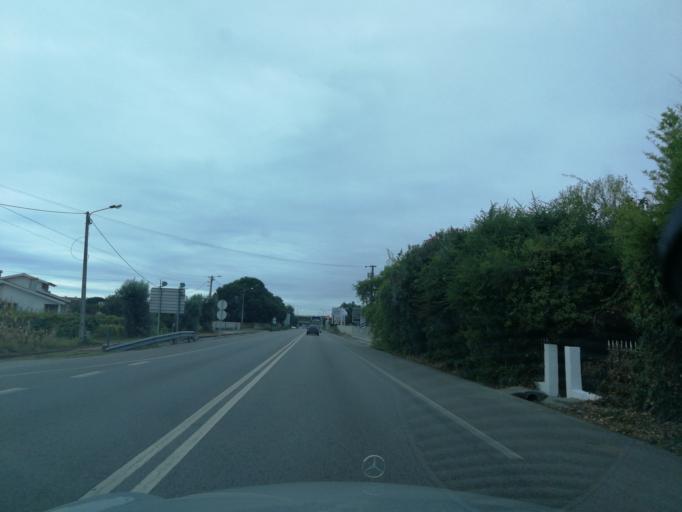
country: PT
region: Aveiro
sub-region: Agueda
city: Valongo
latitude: 40.6146
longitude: -8.4641
